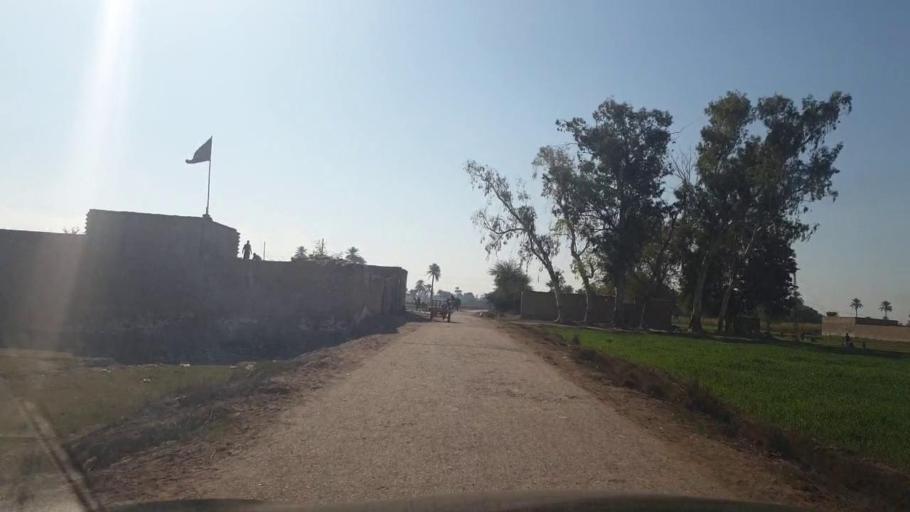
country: PK
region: Sindh
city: Ghotki
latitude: 27.9988
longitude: 69.3273
